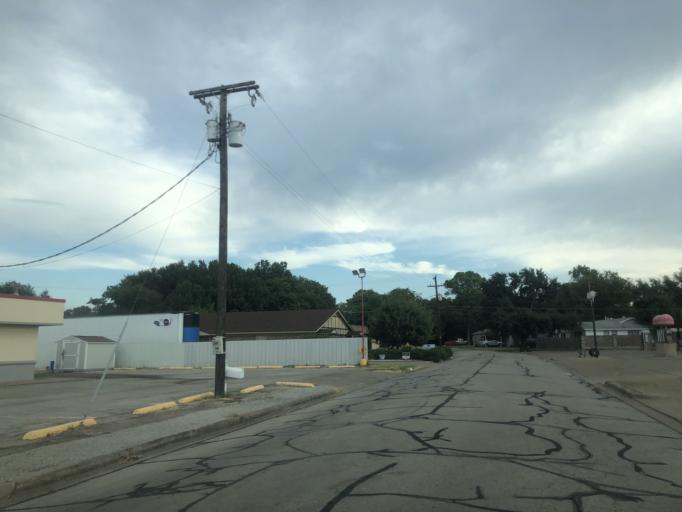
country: US
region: Texas
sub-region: Tarrant County
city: Hurst
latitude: 32.8238
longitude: -97.1598
